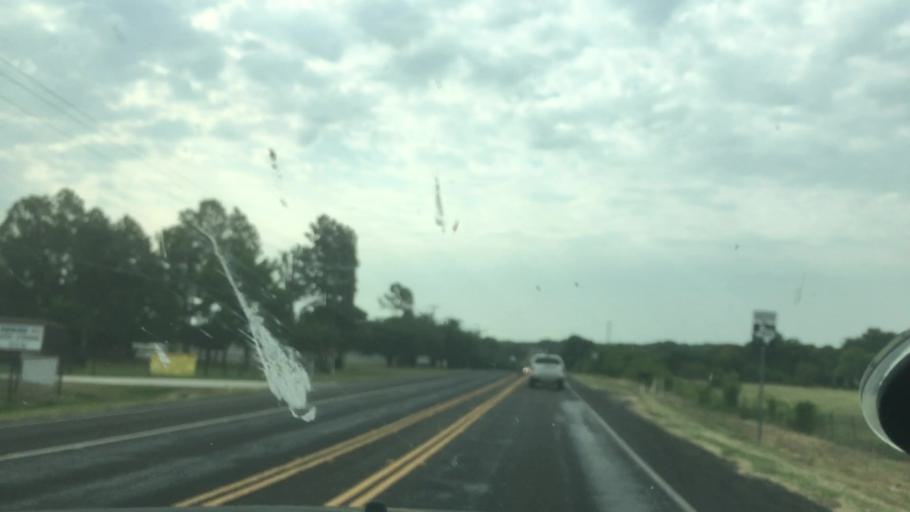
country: US
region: Texas
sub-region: Grayson County
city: Pottsboro
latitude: 33.7960
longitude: -96.6117
